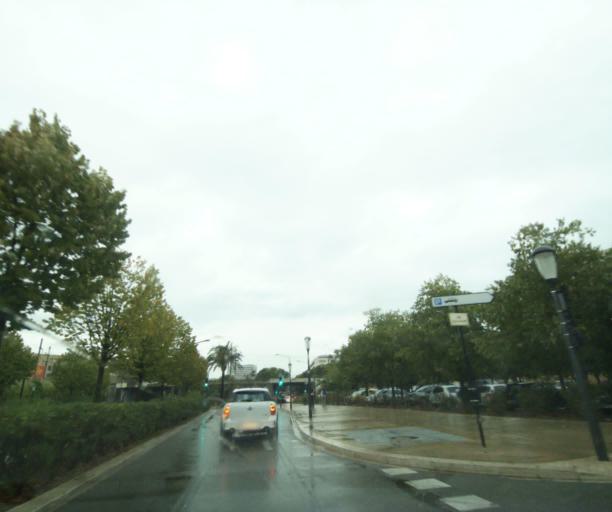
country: FR
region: Languedoc-Roussillon
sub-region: Departement du Gard
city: Nimes
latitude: 43.8238
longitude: 4.3544
